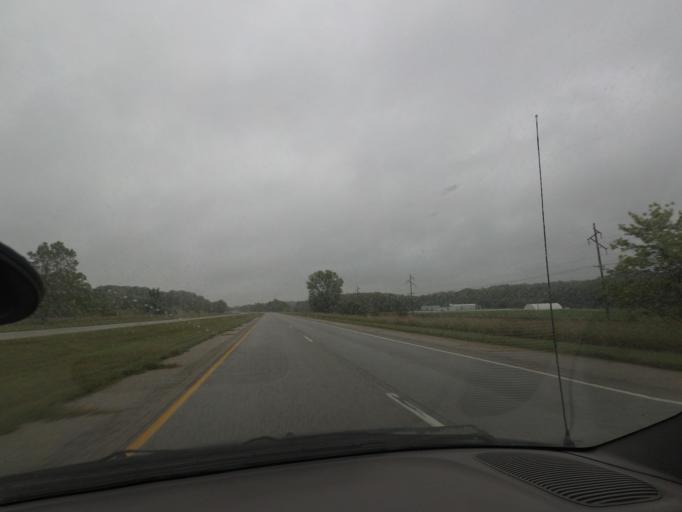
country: US
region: Illinois
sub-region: Pike County
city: Barry
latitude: 39.7141
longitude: -91.0834
